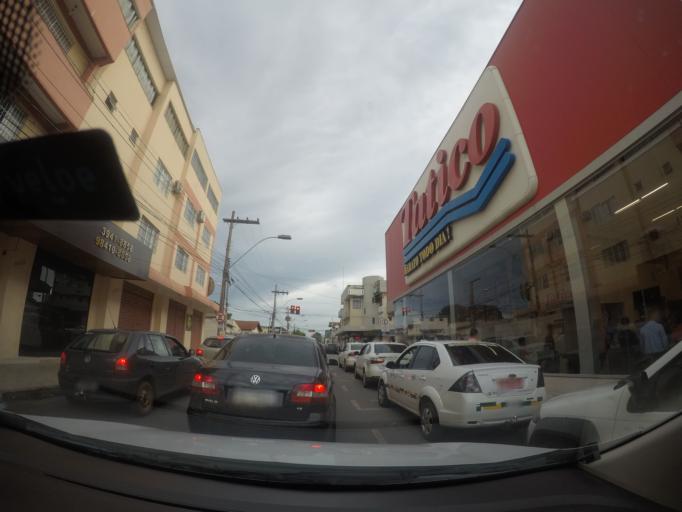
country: BR
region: Goias
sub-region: Goiania
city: Goiania
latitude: -16.6674
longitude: -49.2859
